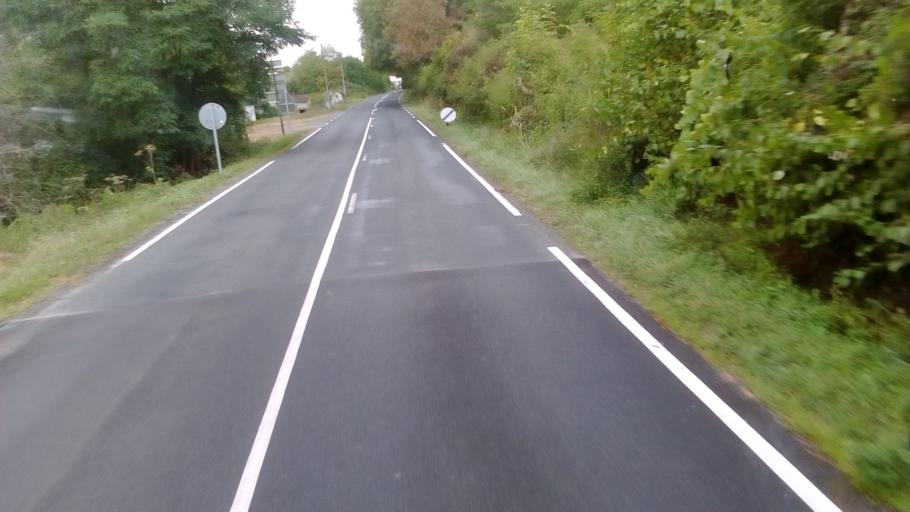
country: FR
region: Bourgogne
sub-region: Departement de Saone-et-Loire
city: La Motte-Saint-Jean
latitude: 46.4917
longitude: 3.9651
